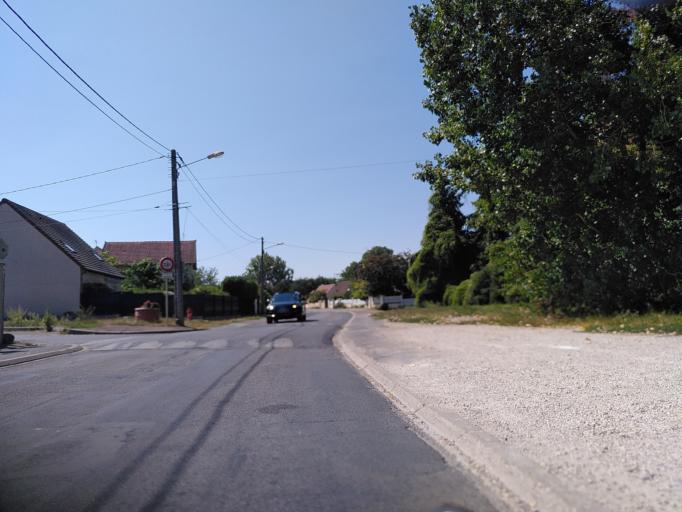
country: FR
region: Ile-de-France
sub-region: Departement de l'Essonne
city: Saint-Germain-les-Arpajon
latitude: 48.6004
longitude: 2.2660
